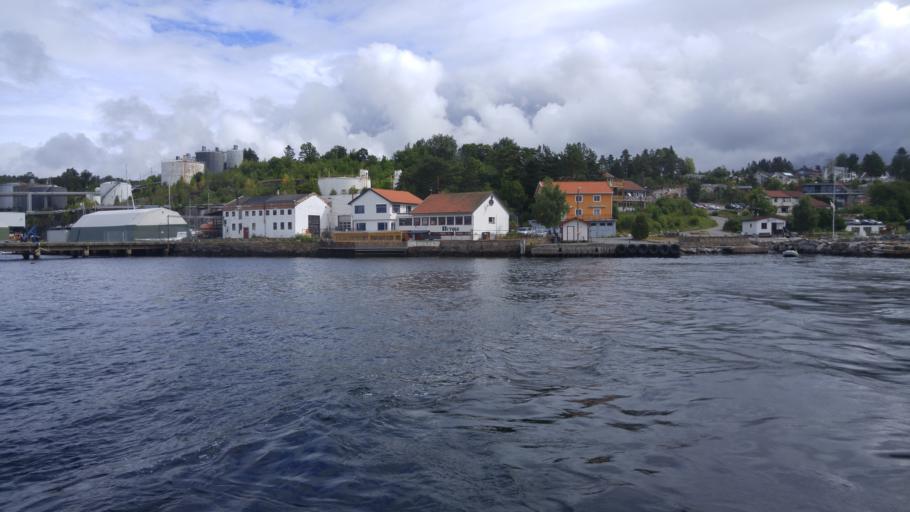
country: NO
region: Akershus
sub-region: Nesodden
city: Fagerstrand
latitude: 59.7336
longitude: 10.5850
